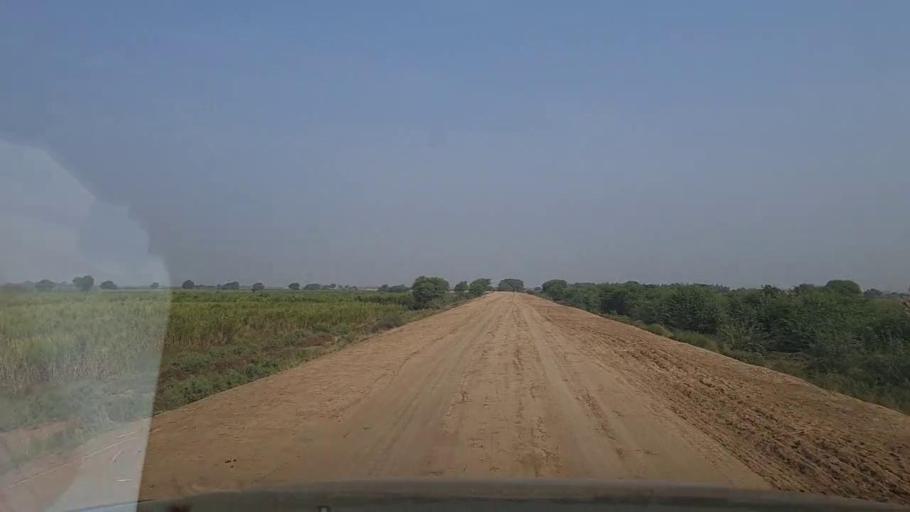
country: PK
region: Sindh
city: Bulri
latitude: 24.9842
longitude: 68.2938
